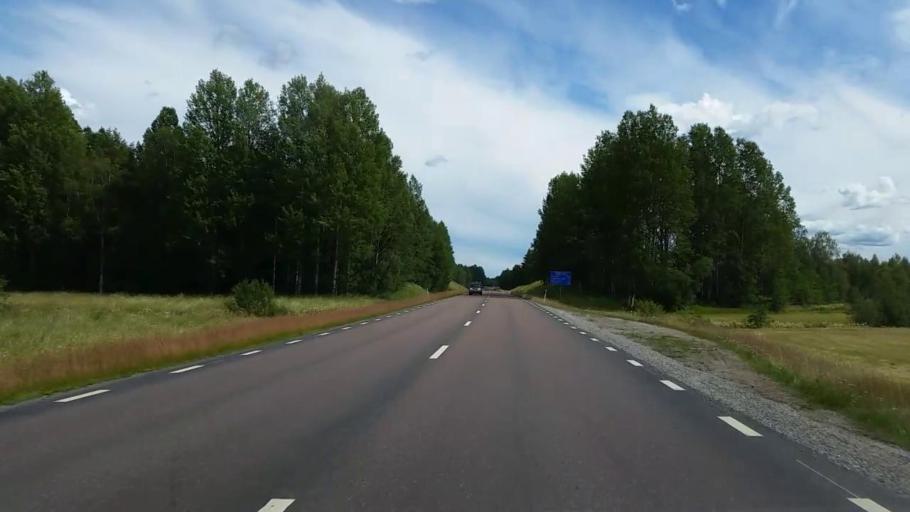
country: SE
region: Gaevleborg
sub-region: Ovanakers Kommun
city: Edsbyn
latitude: 61.3705
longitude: 15.8546
